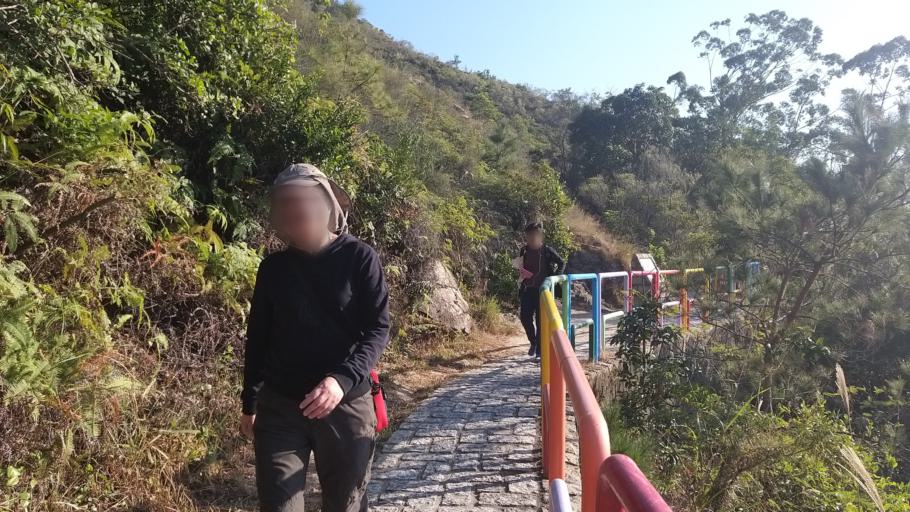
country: HK
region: Tuen Mun
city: Tuen Mun
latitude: 22.3986
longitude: 113.9836
